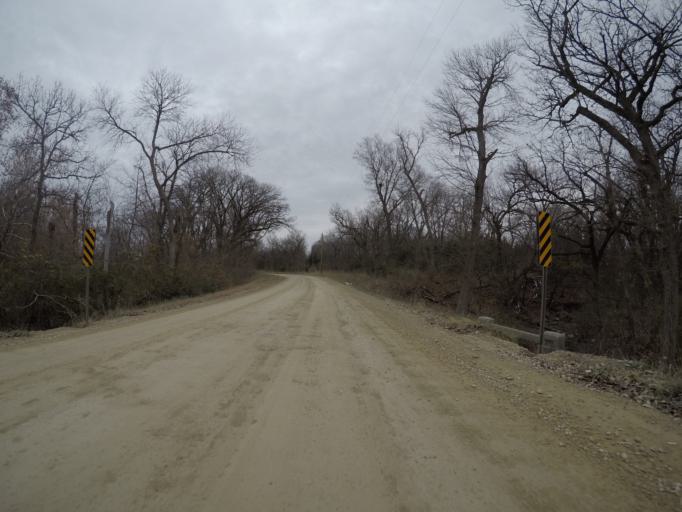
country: US
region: Kansas
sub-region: Riley County
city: Manhattan
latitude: 39.1894
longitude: -96.6579
